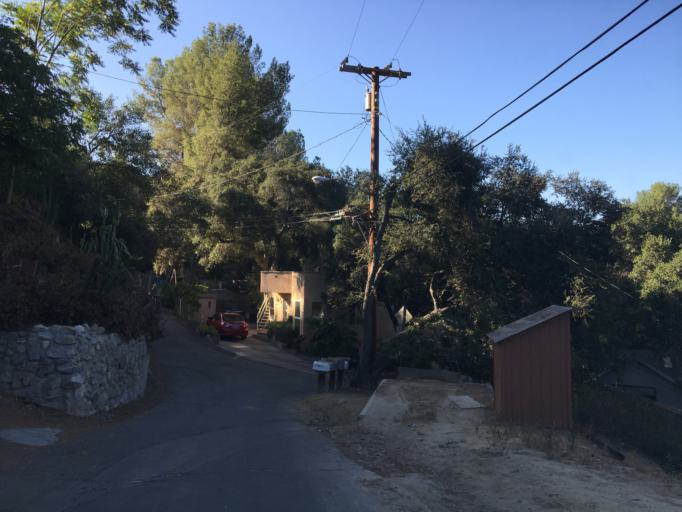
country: US
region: California
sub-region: Los Angeles County
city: San Fernando
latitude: 34.2914
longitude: -118.3754
